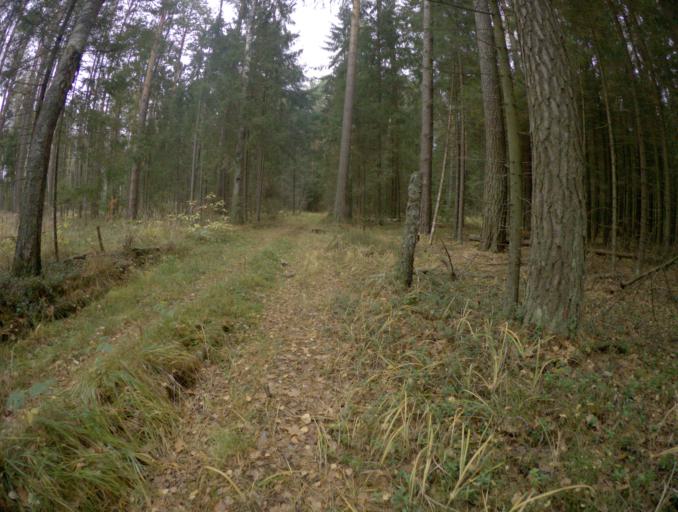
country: RU
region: Vladimir
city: Orgtrud
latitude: 56.1052
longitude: 40.6040
